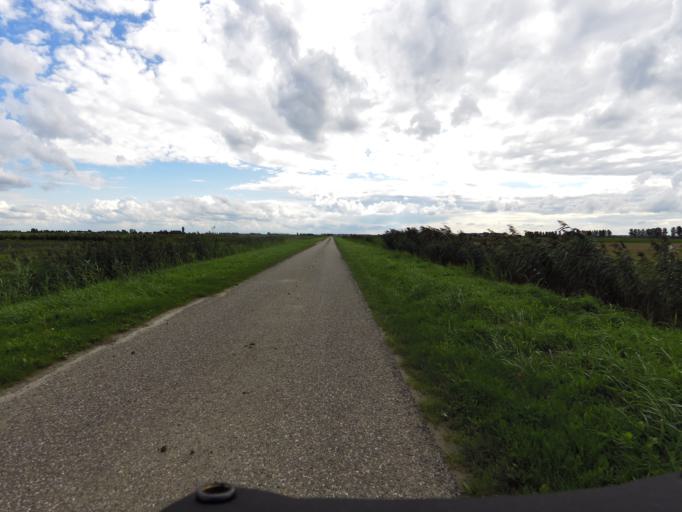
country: NL
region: South Holland
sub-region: Gemeente Goeree-Overflakkee
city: Middelharnis
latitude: 51.7163
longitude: 4.2427
